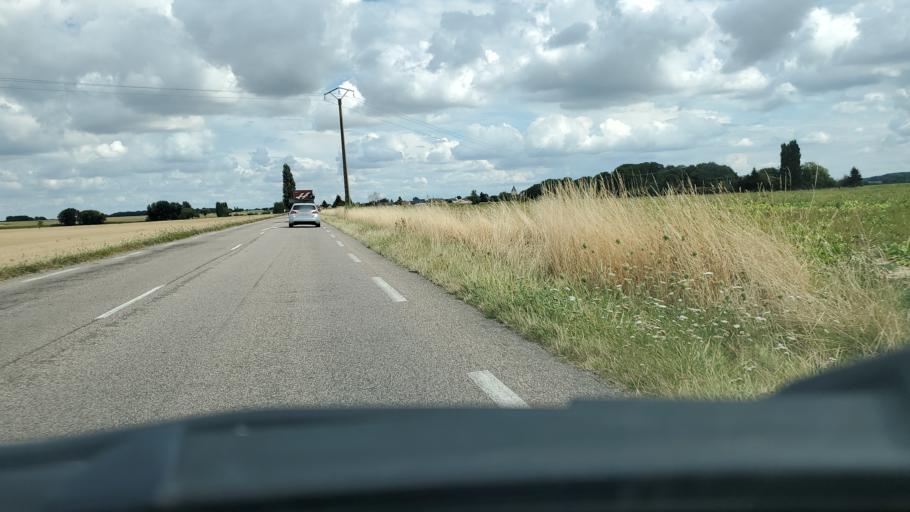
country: FR
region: Ile-de-France
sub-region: Departement de Seine-et-Marne
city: La Chapelle-sur-Crecy
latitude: 48.8908
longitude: 2.9485
